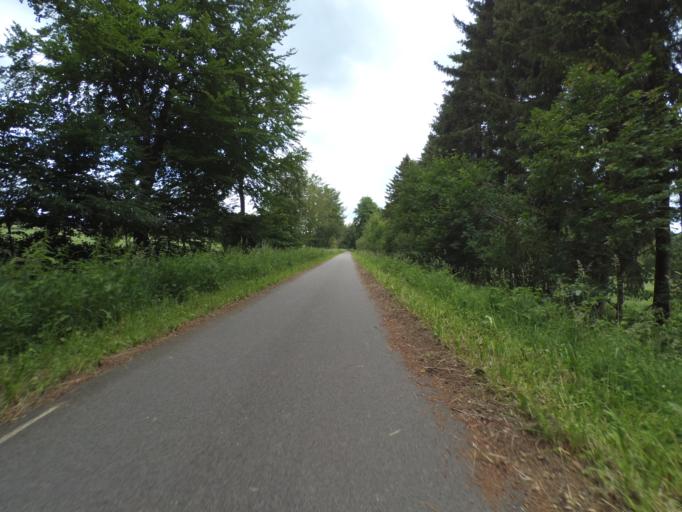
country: DE
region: North Rhine-Westphalia
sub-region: Regierungsbezirk Koln
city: Monschau
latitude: 50.5797
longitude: 6.2392
